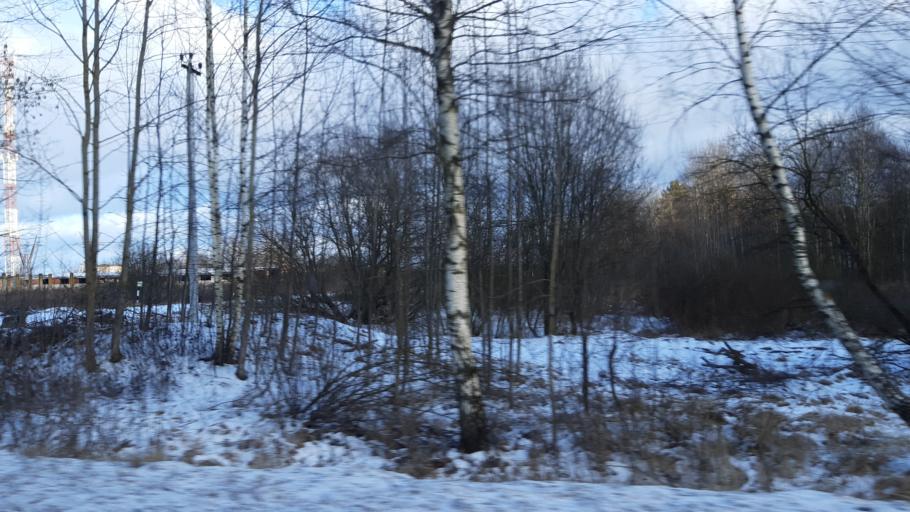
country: RU
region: Moskovskaya
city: Noginsk-9
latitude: 56.0470
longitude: 38.5518
